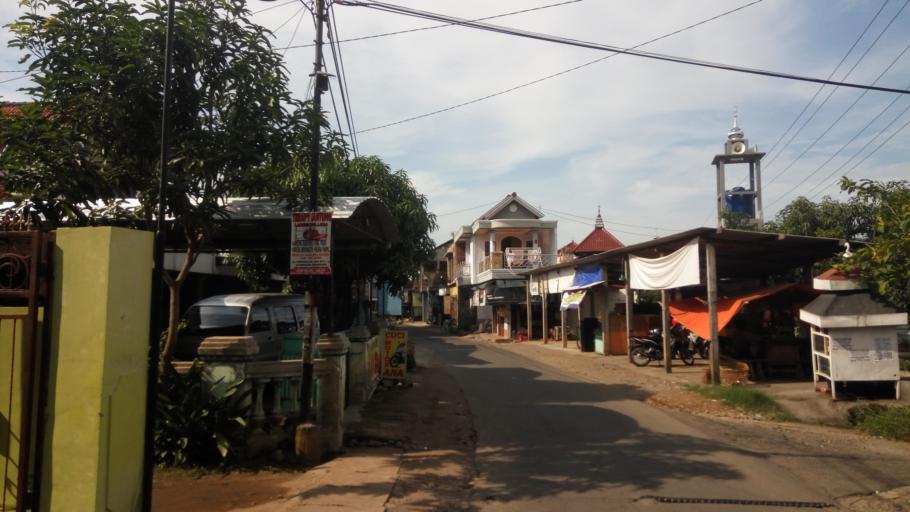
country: ID
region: Central Java
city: Ungaran
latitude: -7.1488
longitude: 110.4125
